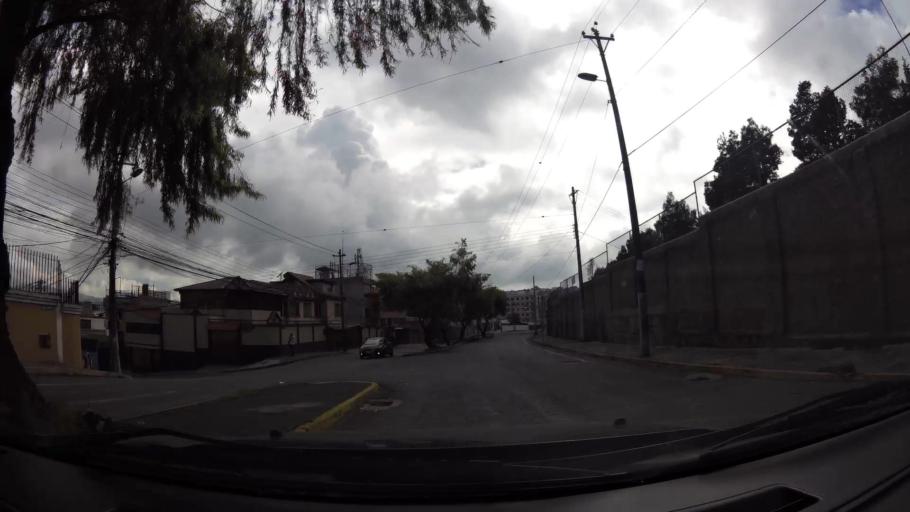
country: EC
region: Pichincha
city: Quito
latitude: -0.1582
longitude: -78.4729
